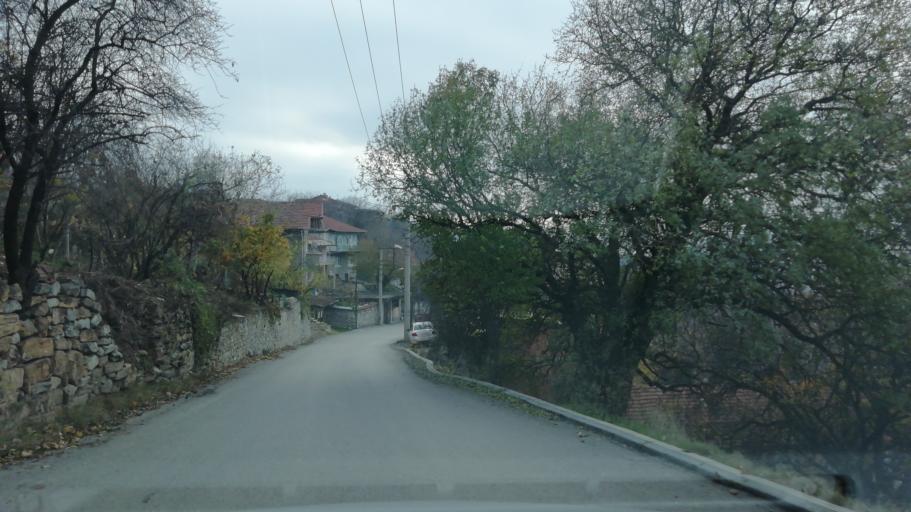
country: TR
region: Karabuk
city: Karabuk
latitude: 41.2181
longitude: 32.6279
